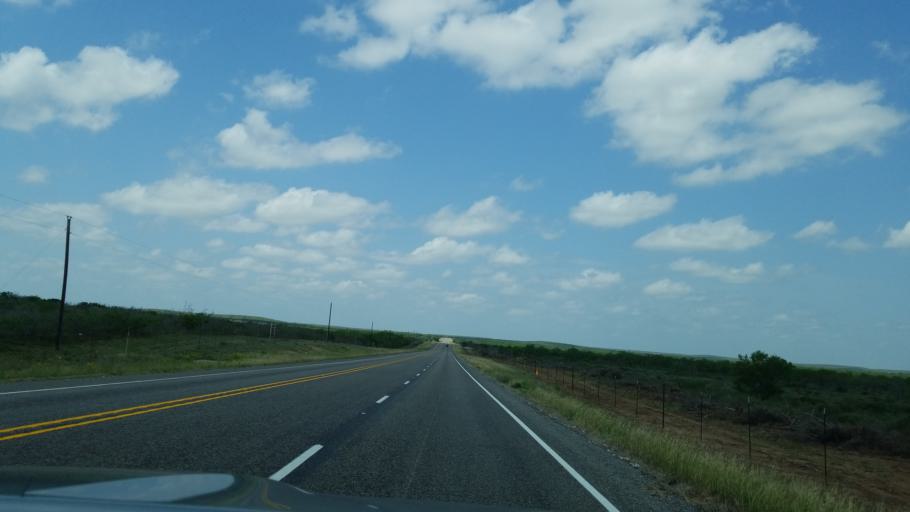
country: US
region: Texas
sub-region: Frio County
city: Pearsall
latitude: 28.9445
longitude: -99.3054
